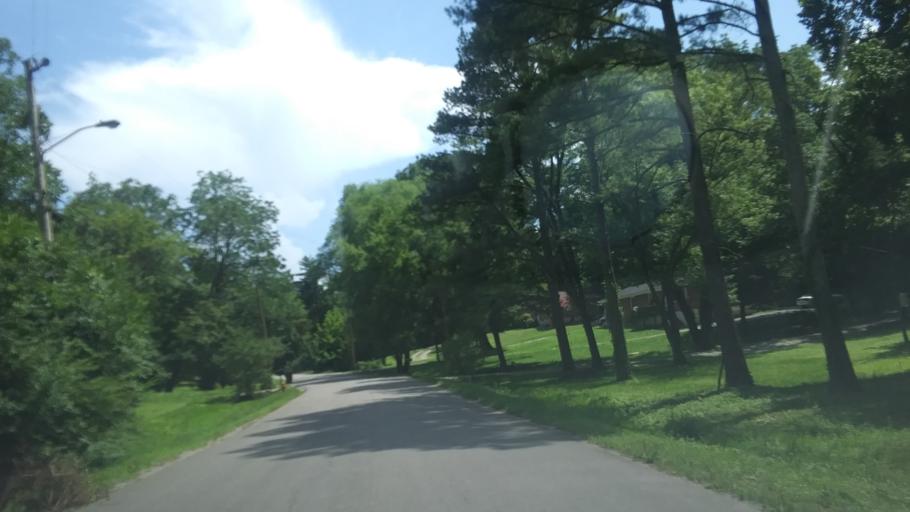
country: US
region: Tennessee
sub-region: Davidson County
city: Oak Hill
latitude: 36.0752
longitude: -86.7136
